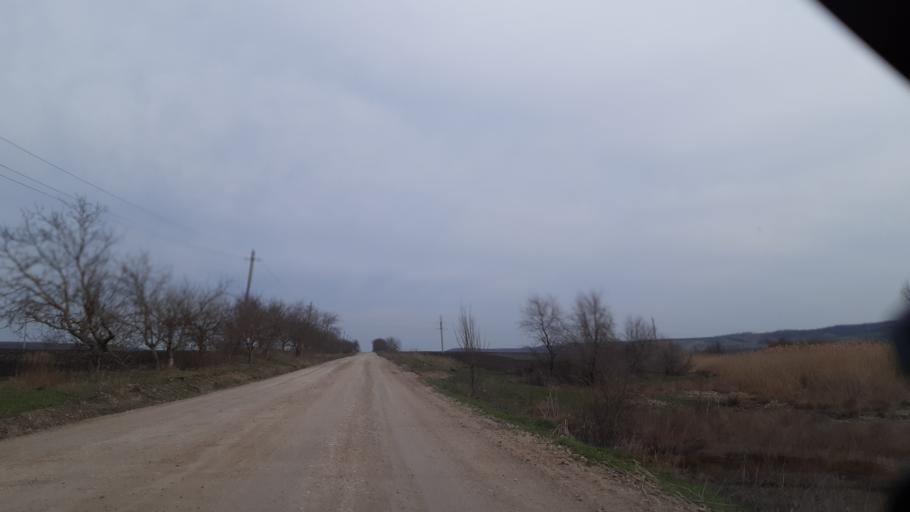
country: MD
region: Soldanesti
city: Soldanesti
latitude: 47.7037
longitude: 28.7172
